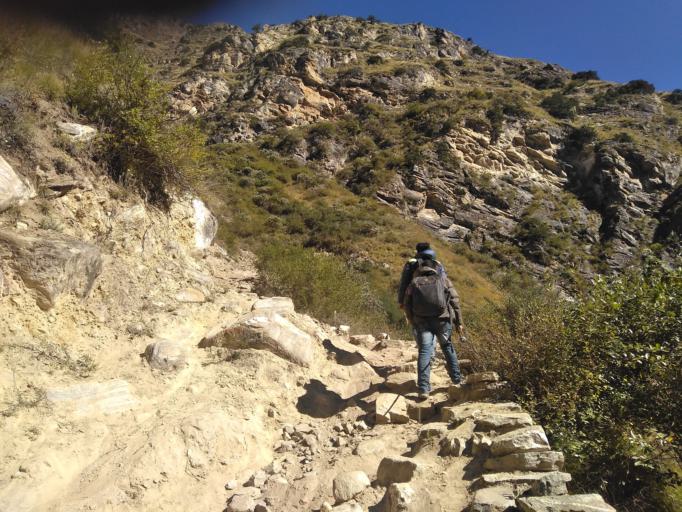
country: NP
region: Western Region
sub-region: Dhawalagiri Zone
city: Jomsom
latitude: 28.9337
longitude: 83.0472
